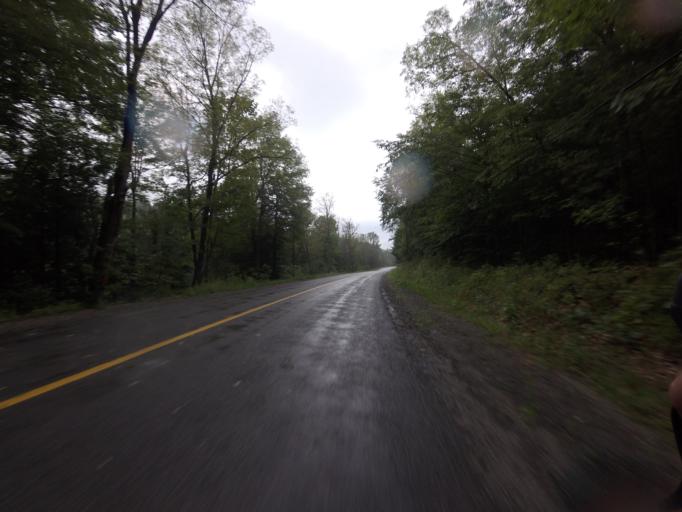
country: CA
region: Ontario
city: Perth
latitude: 45.0545
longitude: -76.6004
